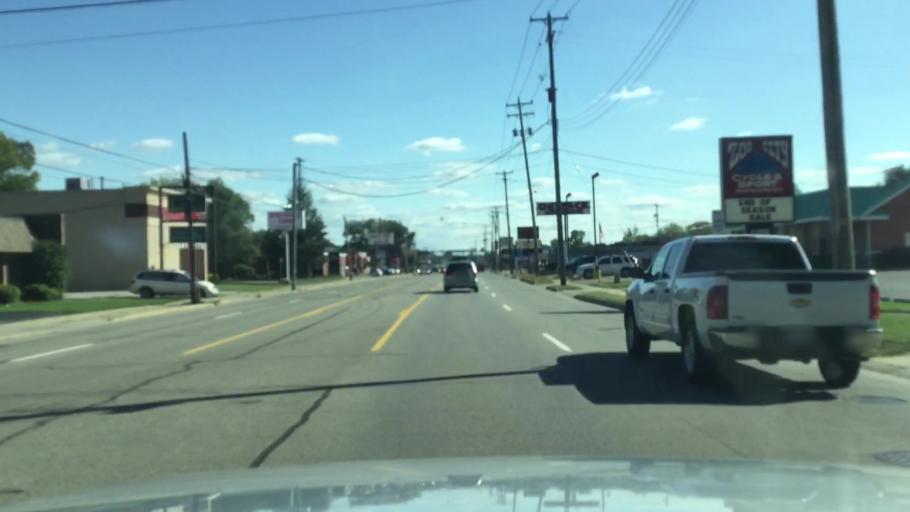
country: US
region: Michigan
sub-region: Kalamazoo County
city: Kalamazoo
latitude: 42.2478
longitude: -85.5897
